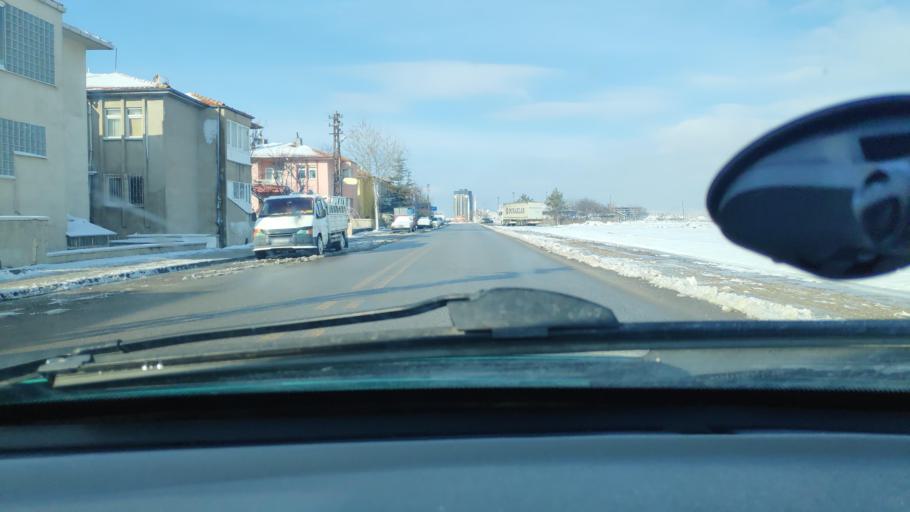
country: TR
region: Ankara
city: Ankara
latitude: 40.0141
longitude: 32.8392
